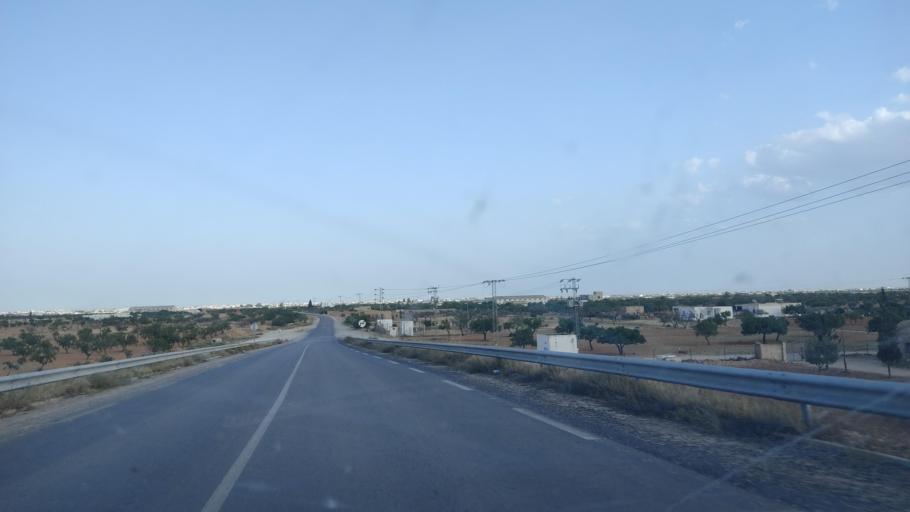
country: TN
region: Safaqis
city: Sfax
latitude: 34.8252
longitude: 10.6436
